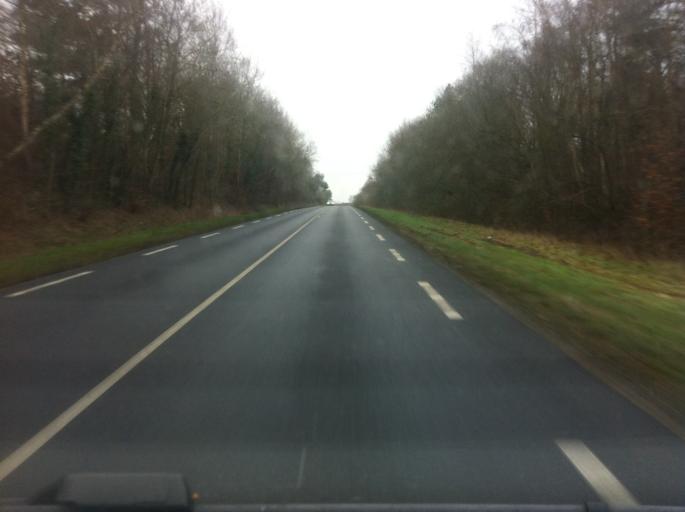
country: FR
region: Haute-Normandie
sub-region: Departement de la Seine-Maritime
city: La Mailleraye-sur-Seine
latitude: 49.4684
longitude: 0.7674
